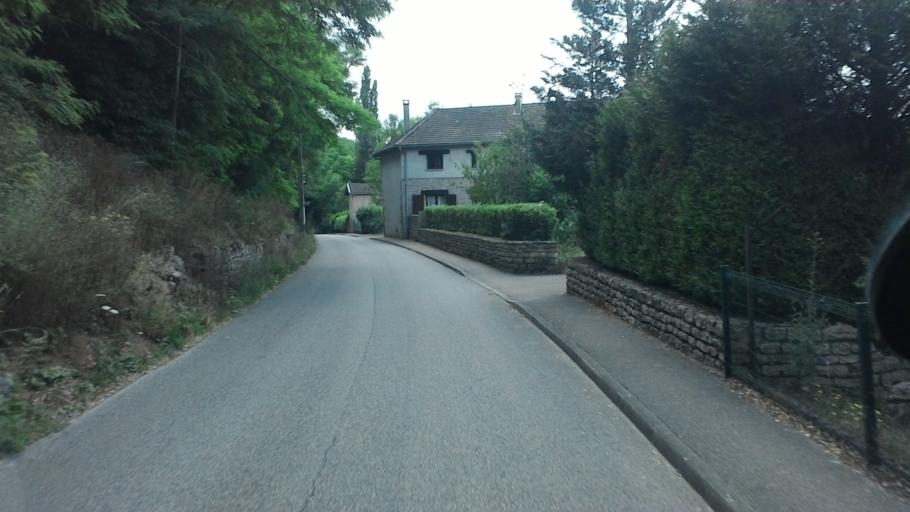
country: FR
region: Rhone-Alpes
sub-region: Departement de l'Ain
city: Villebois
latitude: 45.8534
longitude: 5.4339
